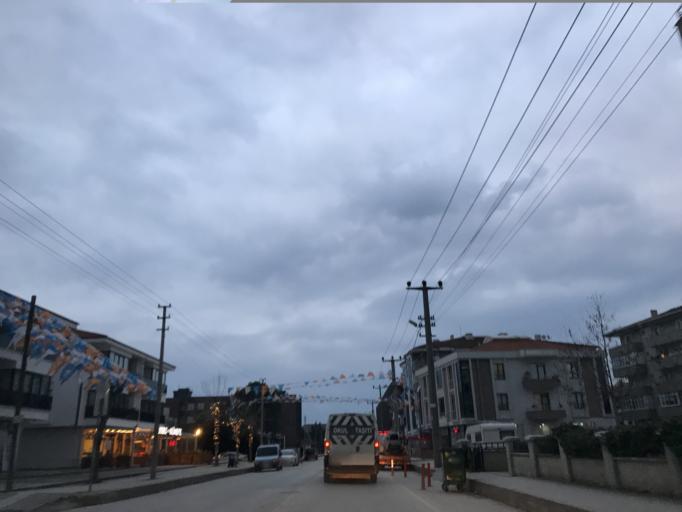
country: TR
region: Yalova
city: Yalova
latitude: 40.6494
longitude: 29.2614
